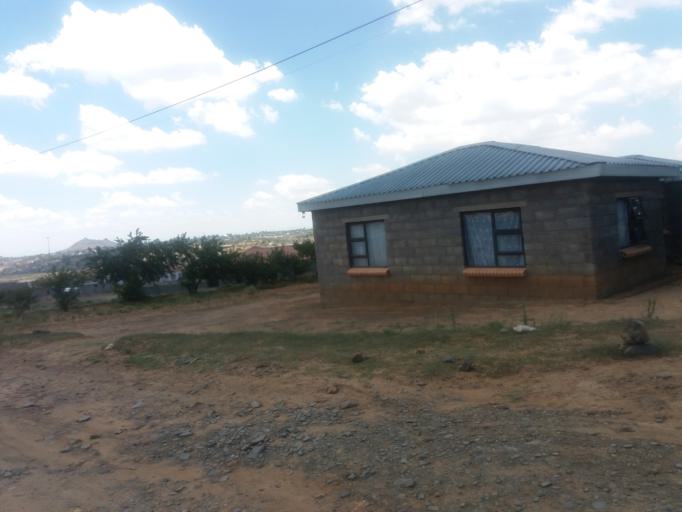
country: LS
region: Maseru
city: Maseru
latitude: -29.3677
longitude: 27.4749
